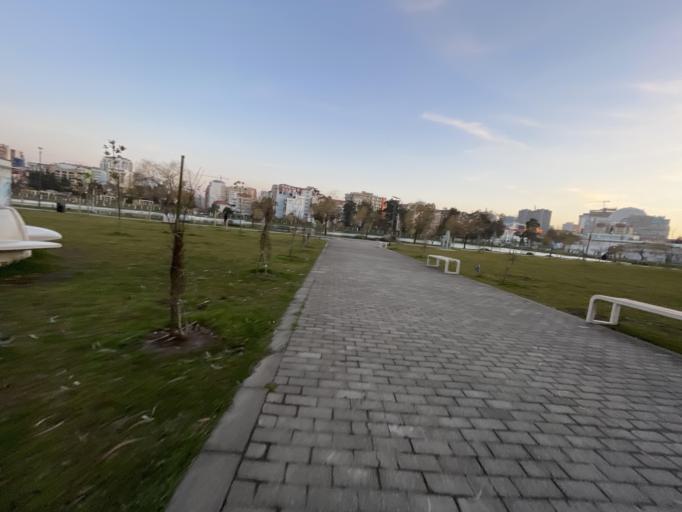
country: GE
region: Ajaria
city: Batumi
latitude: 41.6485
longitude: 41.6254
